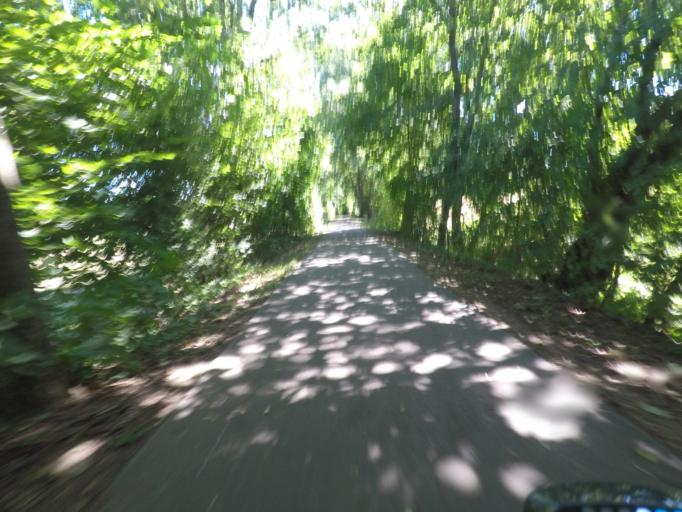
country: DE
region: Schleswig-Holstein
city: Gronwohld
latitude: 53.6346
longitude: 10.3972
